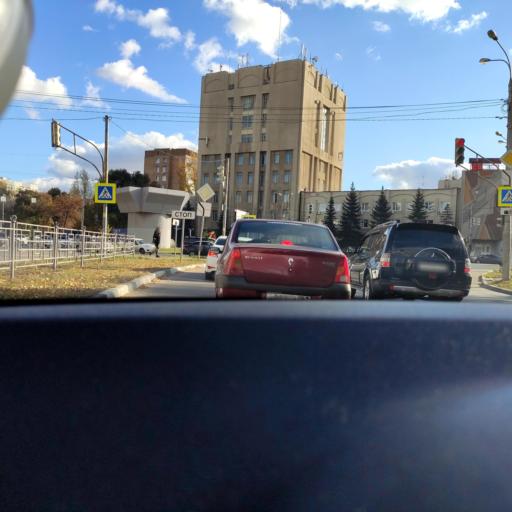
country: RU
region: Samara
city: Samara
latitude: 53.2005
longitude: 50.1634
